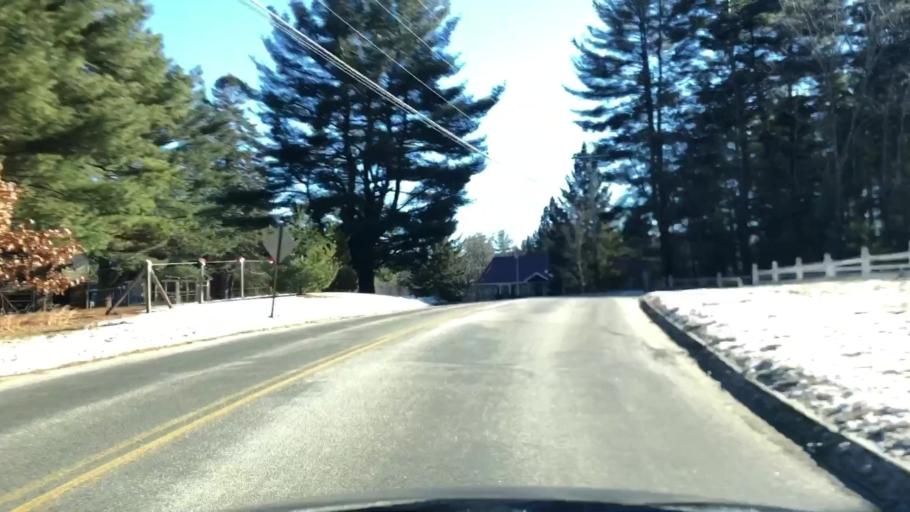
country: US
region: New Hampshire
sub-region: Hillsborough County
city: Milford
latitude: 42.8166
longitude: -71.6568
